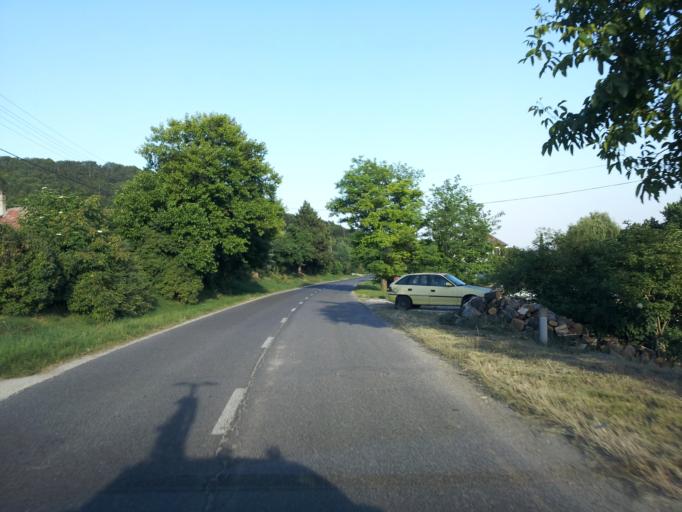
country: HU
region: Fejer
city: Many
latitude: 47.5266
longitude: 18.6034
